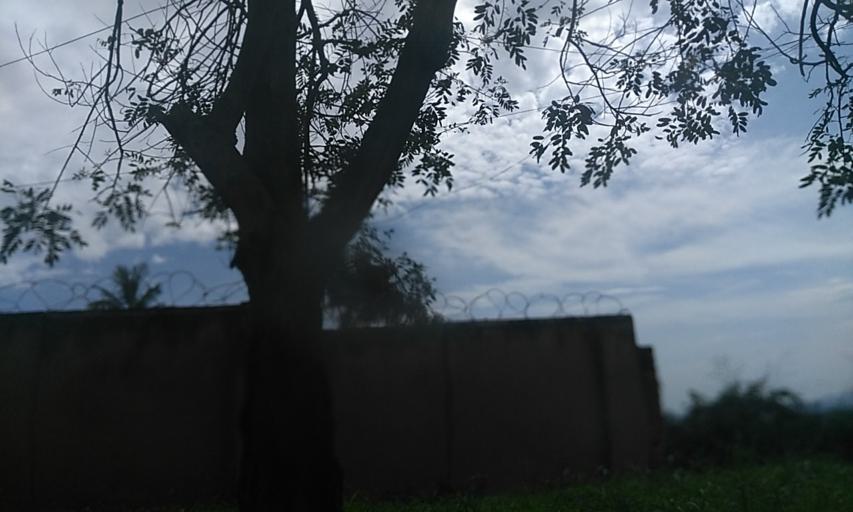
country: UG
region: Central Region
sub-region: Kampala District
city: Kampala
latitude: 0.3322
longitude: 32.5964
